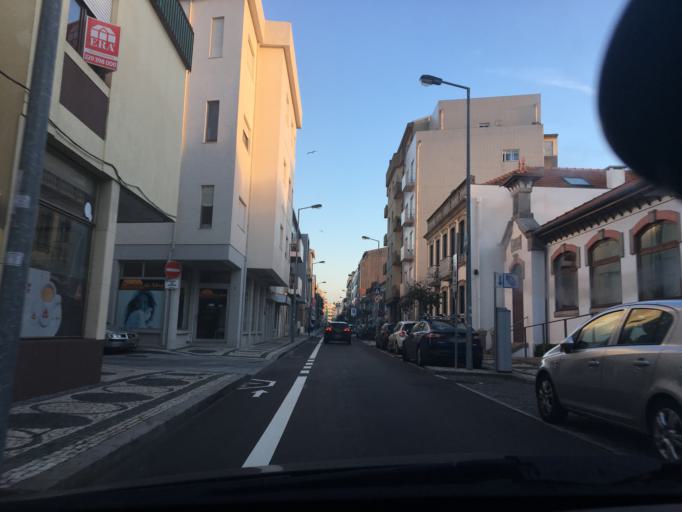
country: PT
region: Porto
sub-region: Matosinhos
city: Matosinhos
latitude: 41.1856
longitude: -8.6911
